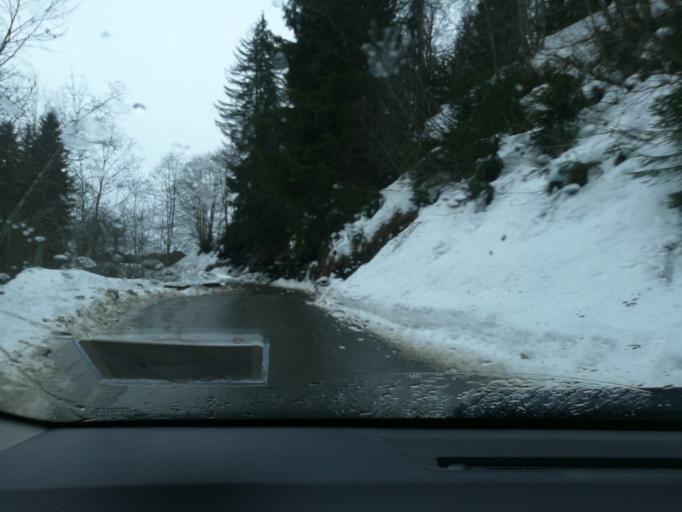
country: FR
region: Rhone-Alpes
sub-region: Departement de la Haute-Savoie
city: Saint-Gervais-les-Bains
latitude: 45.8661
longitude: 6.6913
